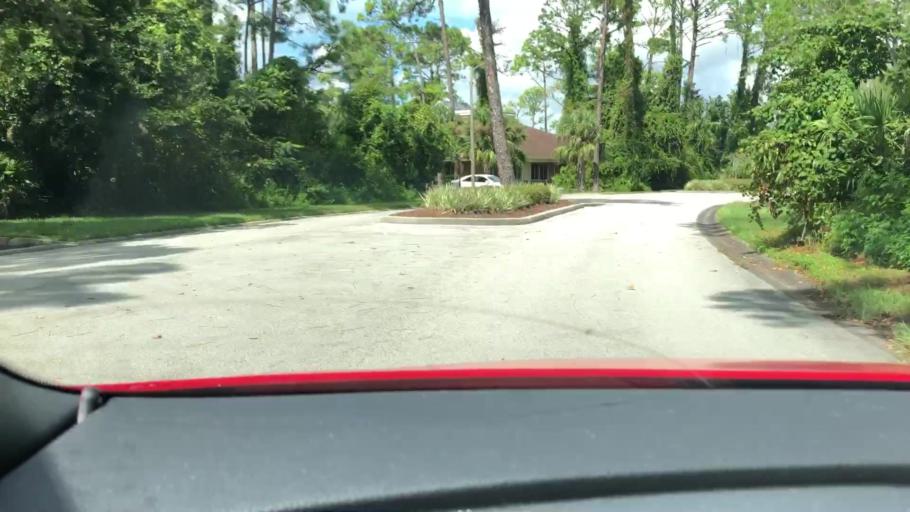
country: US
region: Florida
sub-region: Volusia County
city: Ormond Beach
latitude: 29.2696
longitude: -81.0977
